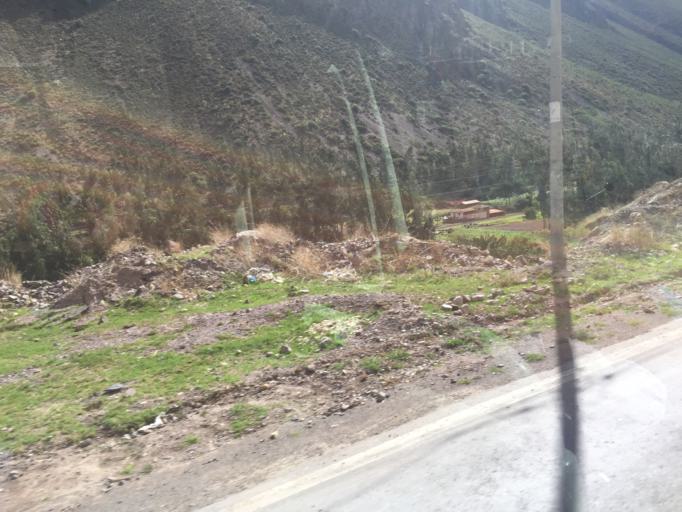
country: PE
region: Cusco
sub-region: Provincia de Urubamba
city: Ollantaytambo
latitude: -13.2662
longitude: -72.2301
